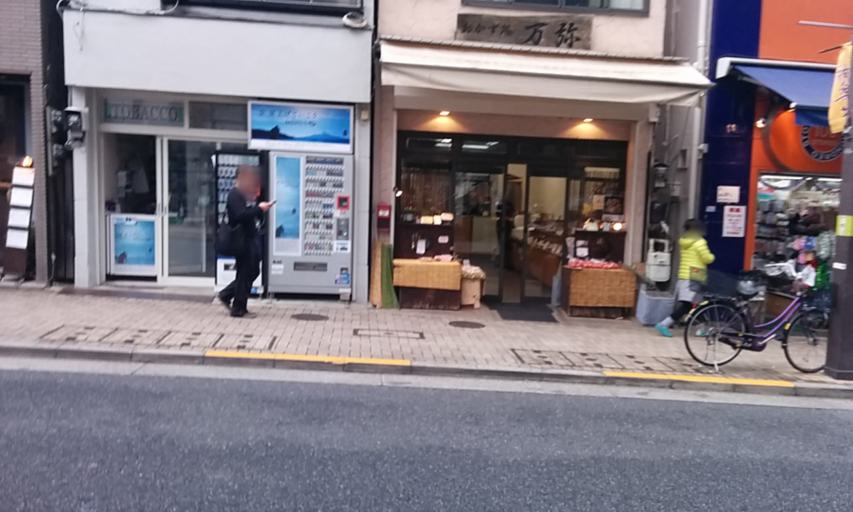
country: JP
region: Tokyo
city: Tokyo
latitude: 35.7031
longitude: 139.7367
